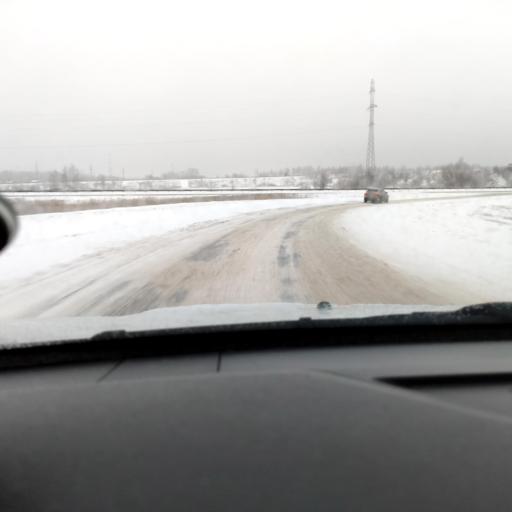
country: RU
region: Samara
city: Smyshlyayevka
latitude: 53.2620
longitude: 50.4761
